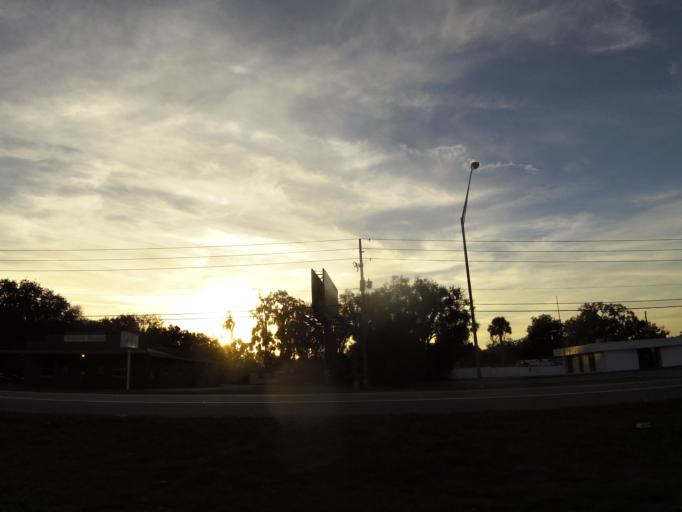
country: US
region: Florida
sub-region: Volusia County
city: De Land Southwest
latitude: 29.0094
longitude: -81.3028
